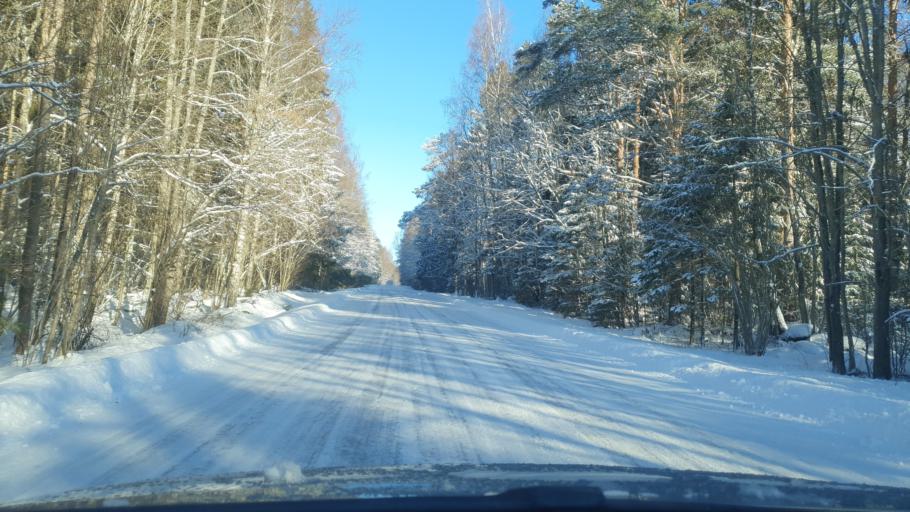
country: EE
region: Harju
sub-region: Kuusalu vald
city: Kuusalu
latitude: 59.5489
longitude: 25.5604
